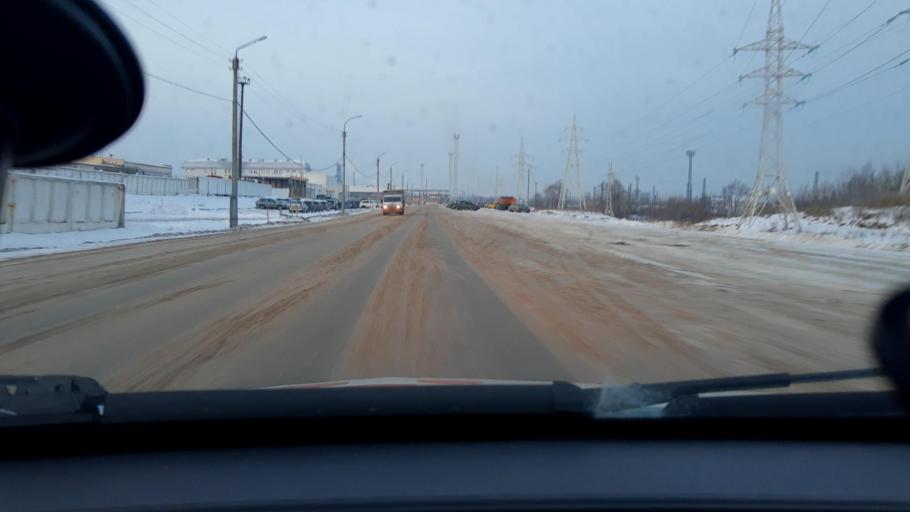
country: RU
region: Bashkortostan
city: Blagoveshchensk
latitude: 54.9218
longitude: 56.0768
